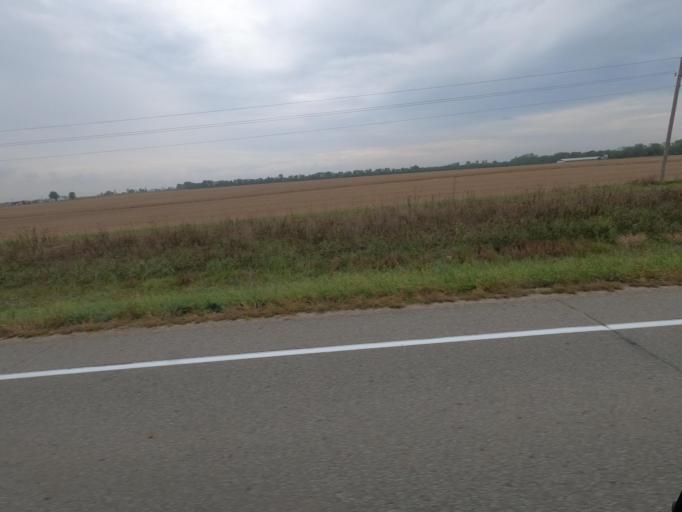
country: US
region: Iowa
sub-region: Van Buren County
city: Keosauqua
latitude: 40.8133
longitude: -91.7714
